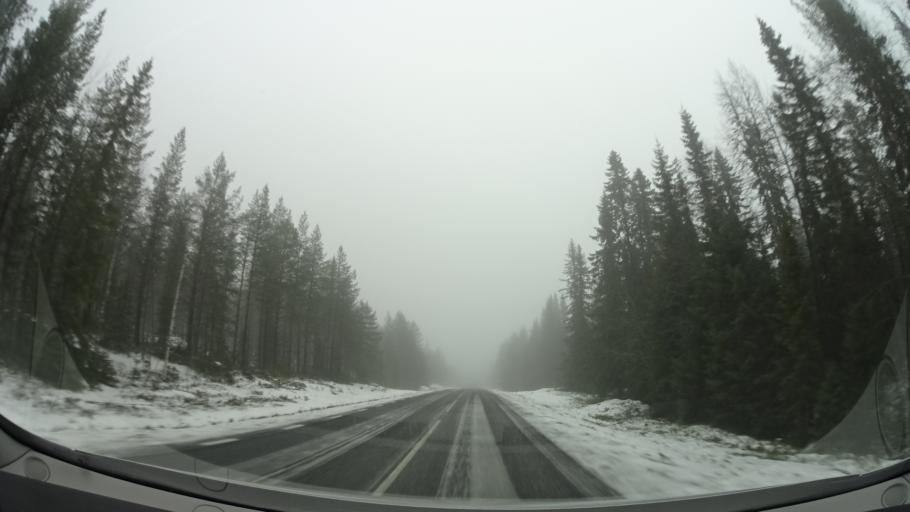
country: SE
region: Vaesterbotten
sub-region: Asele Kommun
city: Insjon
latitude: 64.3494
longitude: 17.8456
